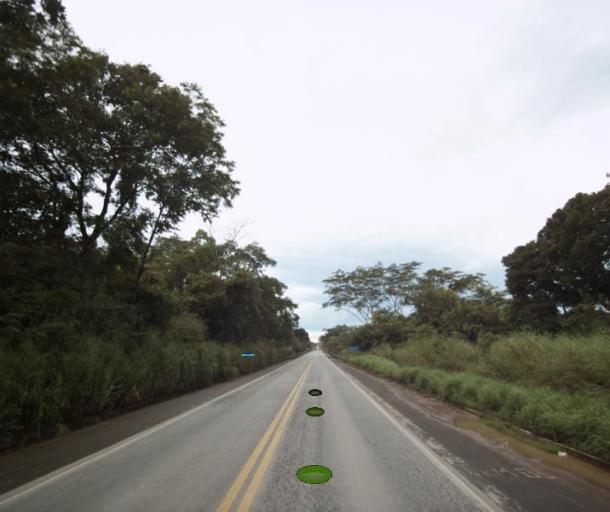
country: BR
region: Goias
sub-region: Porangatu
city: Porangatu
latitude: -13.5529
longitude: -49.0871
